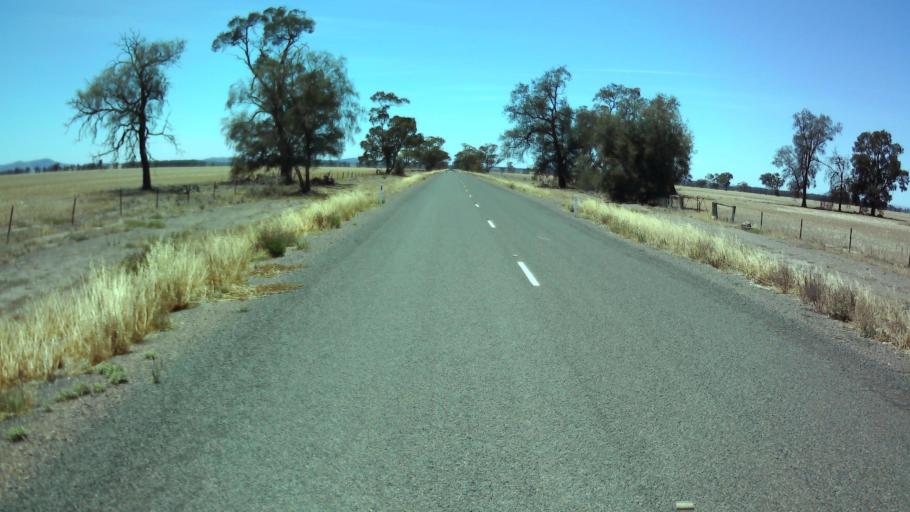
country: AU
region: New South Wales
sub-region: Bland
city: West Wyalong
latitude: -33.6577
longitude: 147.5750
